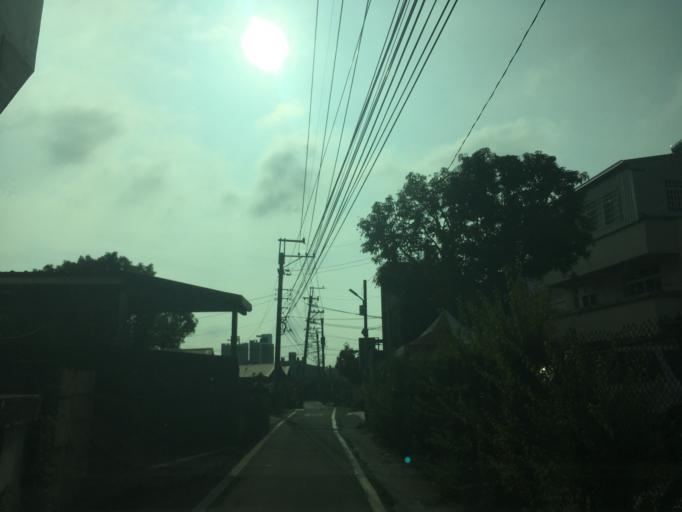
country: TW
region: Taiwan
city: Fengyuan
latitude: 24.2374
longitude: 120.7320
